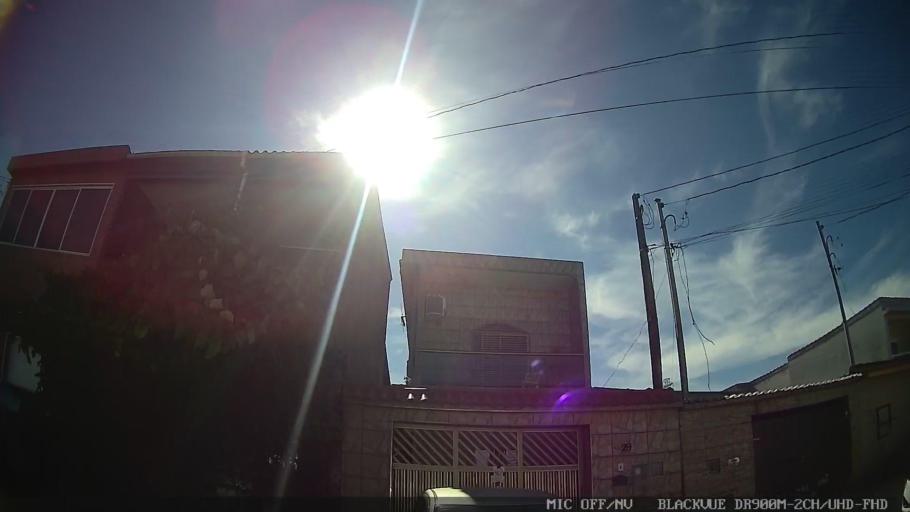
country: BR
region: Sao Paulo
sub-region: Santos
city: Santos
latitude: -23.9358
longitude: -46.2852
